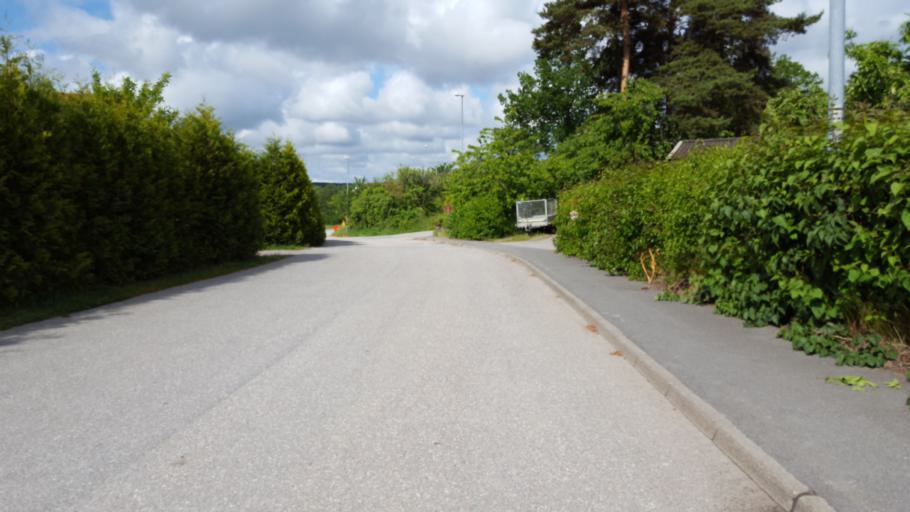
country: SE
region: Stockholm
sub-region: Upplands Vasby Kommun
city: Upplands Vaesby
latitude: 59.5089
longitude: 17.8840
